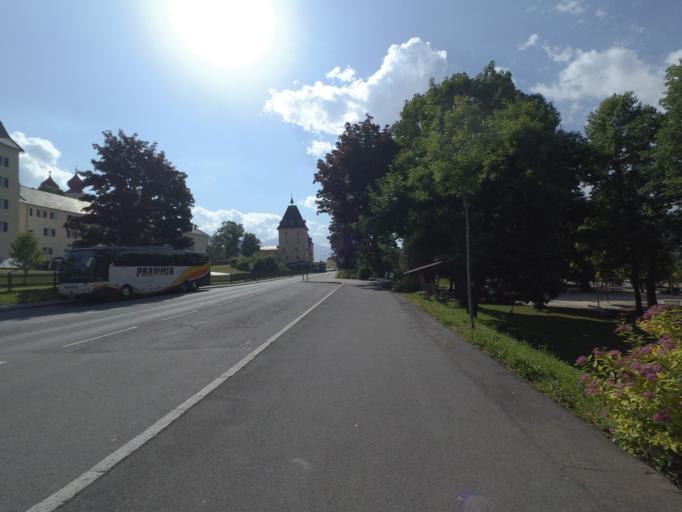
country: AT
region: Carinthia
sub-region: Politischer Bezirk Spittal an der Drau
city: Millstatt
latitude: 46.8040
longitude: 13.5688
